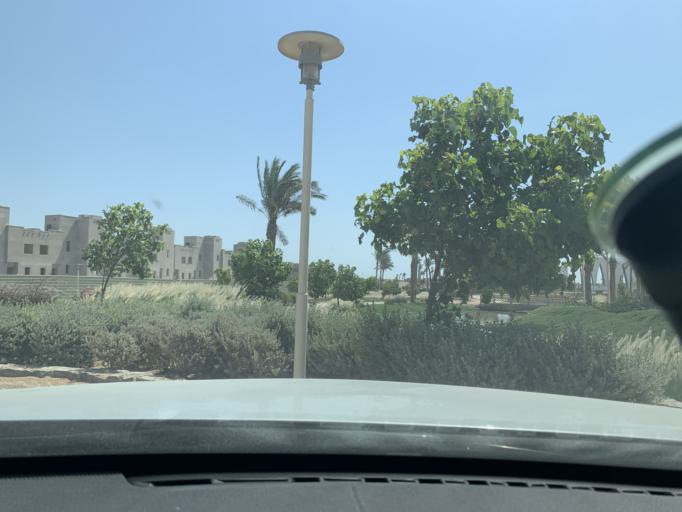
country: EG
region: Red Sea
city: El Gouna
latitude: 27.4037
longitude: 33.6641
